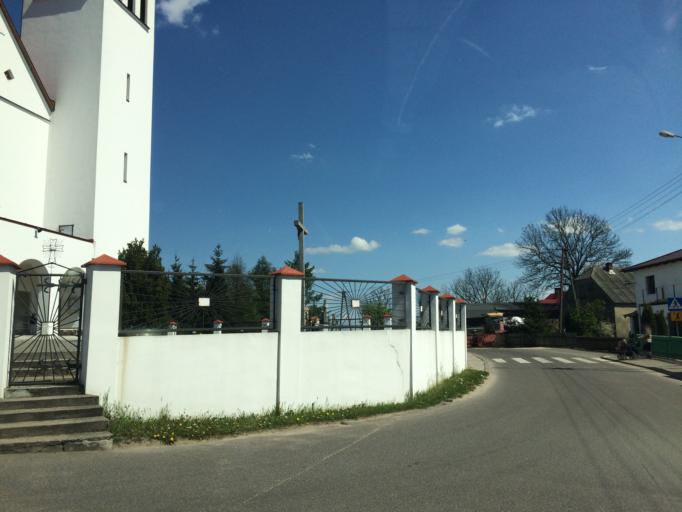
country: PL
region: Warmian-Masurian Voivodeship
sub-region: Powiat nowomiejski
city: Kurzetnik
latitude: 53.3849
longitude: 19.4675
